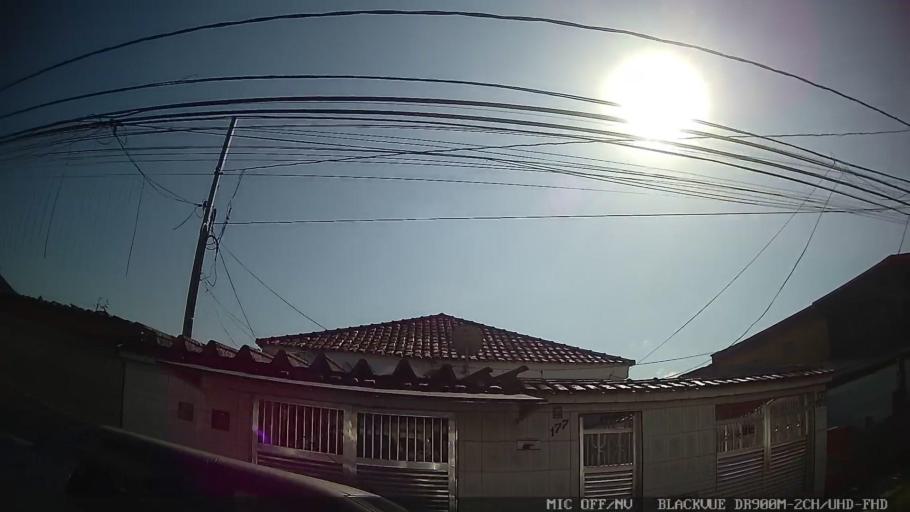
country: BR
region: Sao Paulo
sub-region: Santos
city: Santos
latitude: -23.9437
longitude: -46.2974
